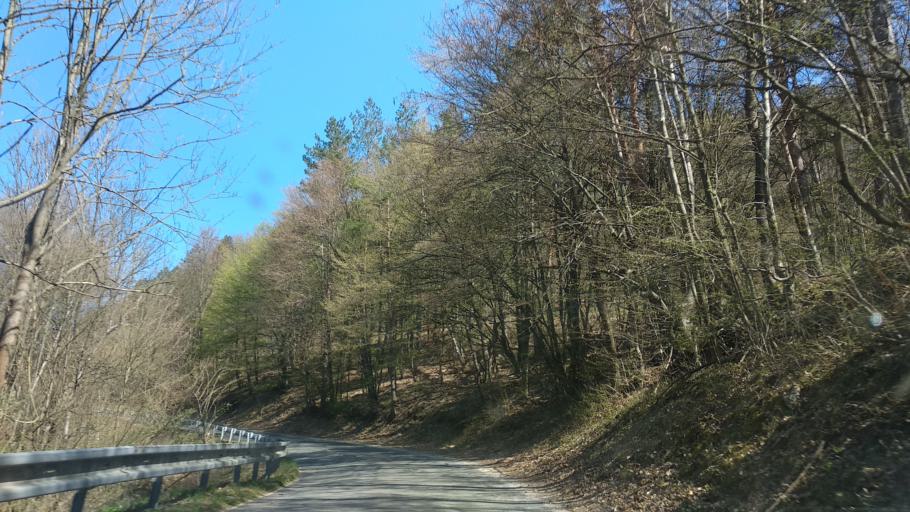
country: SK
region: Nitriansky
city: Trencianske Teplice
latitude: 48.8616
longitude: 18.1785
